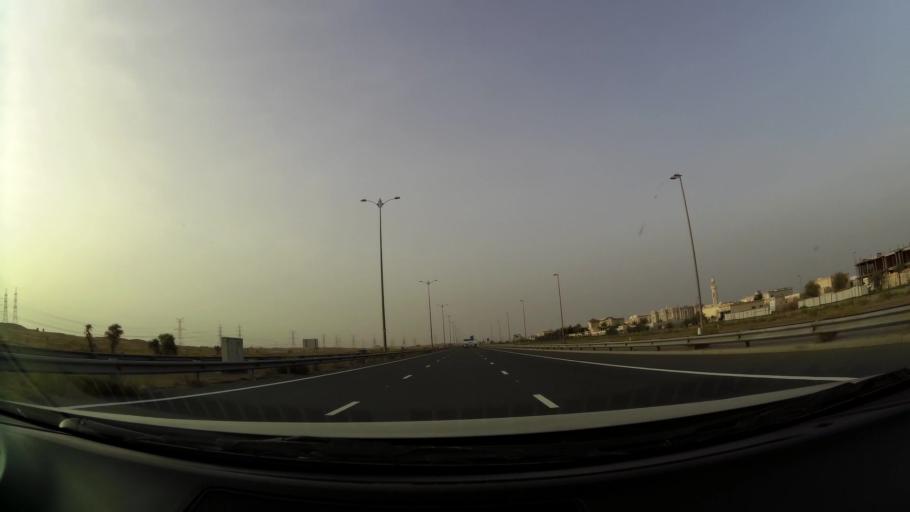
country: OM
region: Al Buraimi
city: Al Buraymi
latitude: 24.3063
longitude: 55.7451
